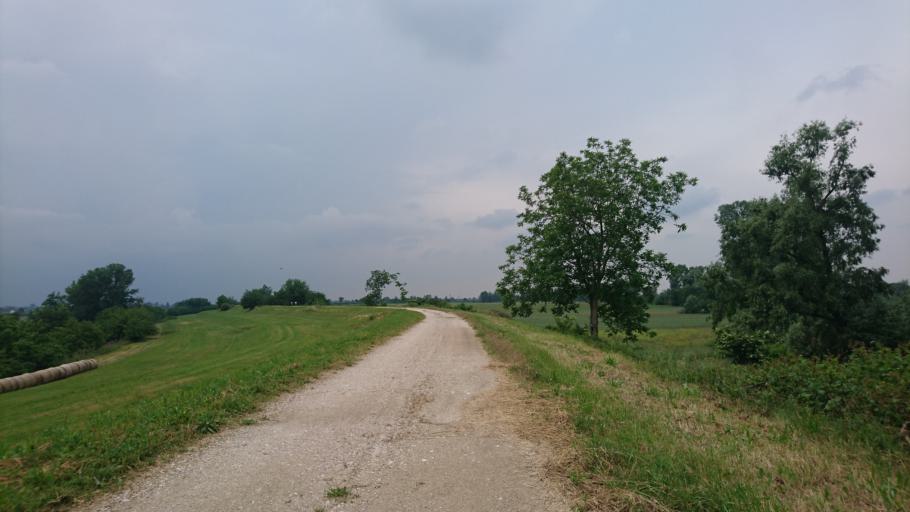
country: IT
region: Veneto
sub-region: Provincia di Padova
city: Masi
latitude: 45.1162
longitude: 11.5166
